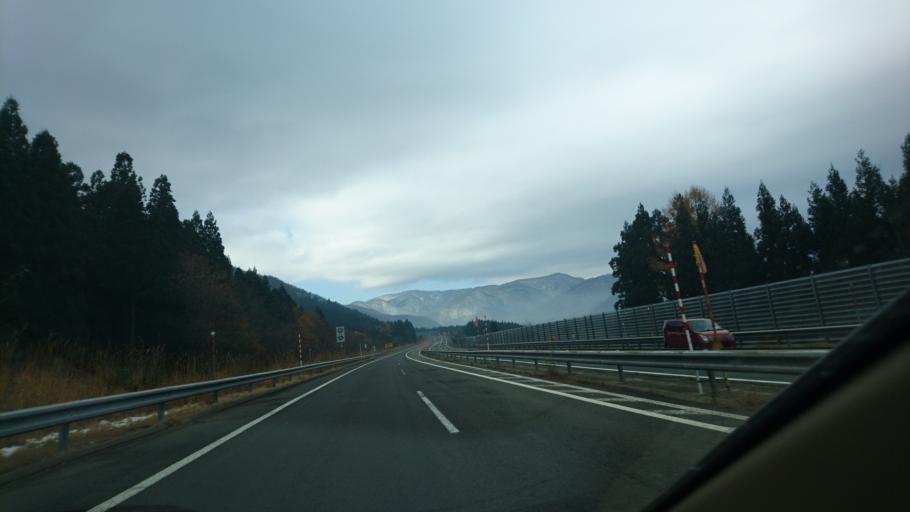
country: JP
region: Iwate
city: Kitakami
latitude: 39.2949
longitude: 140.9472
